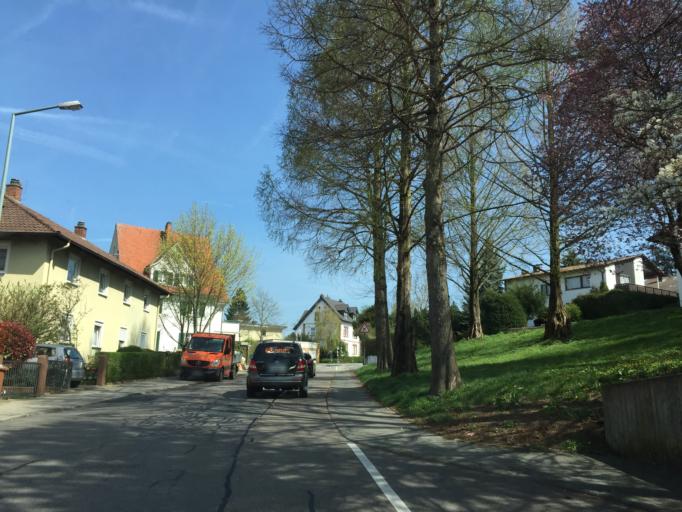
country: DE
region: Baden-Wuerttemberg
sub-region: Karlsruhe Region
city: Weinheim
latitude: 49.5414
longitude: 8.6629
